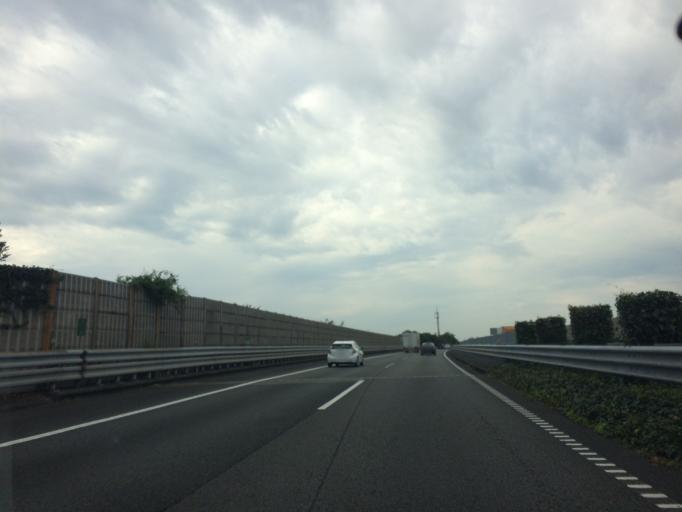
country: JP
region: Shizuoka
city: Yaizu
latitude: 34.8741
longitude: 138.2938
